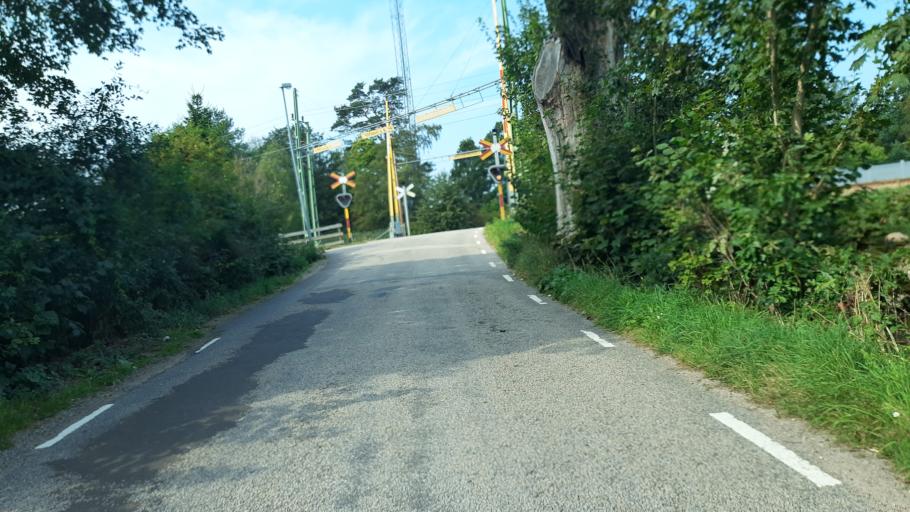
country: SE
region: Blekinge
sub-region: Karlskrona Kommun
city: Nattraby
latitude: 56.2267
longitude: 15.4225
